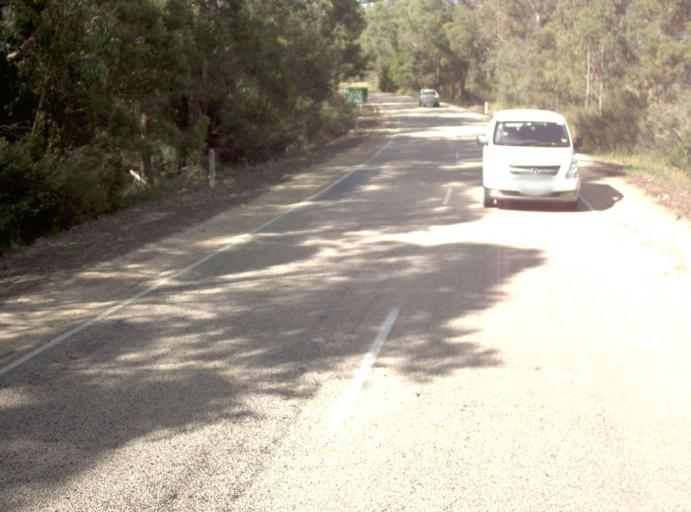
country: AU
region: Victoria
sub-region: East Gippsland
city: Lakes Entrance
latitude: -37.5347
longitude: 148.1495
